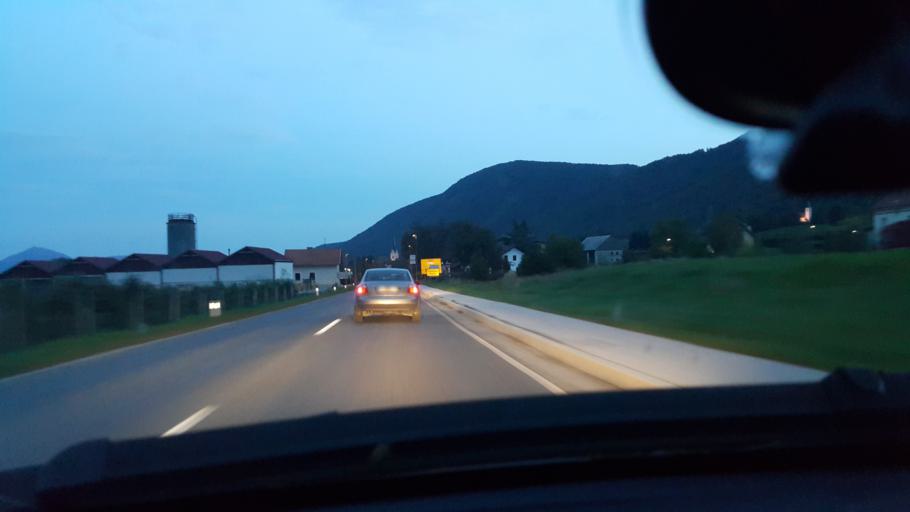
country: SI
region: Slovenska Konjice
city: Slovenske Konjice
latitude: 46.3438
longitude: 15.4117
